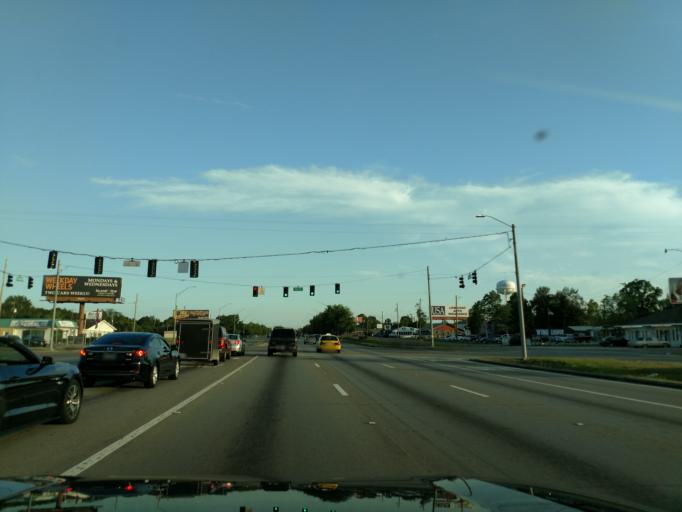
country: US
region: Mississippi
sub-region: Harrison County
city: West Gulfport
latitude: 30.4093
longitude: -89.0930
